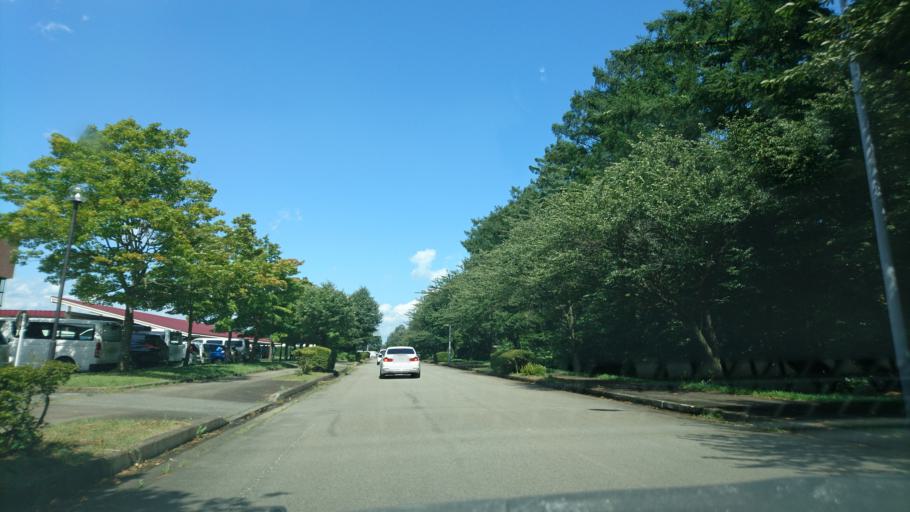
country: JP
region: Iwate
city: Morioka-shi
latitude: 39.8085
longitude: 141.1329
